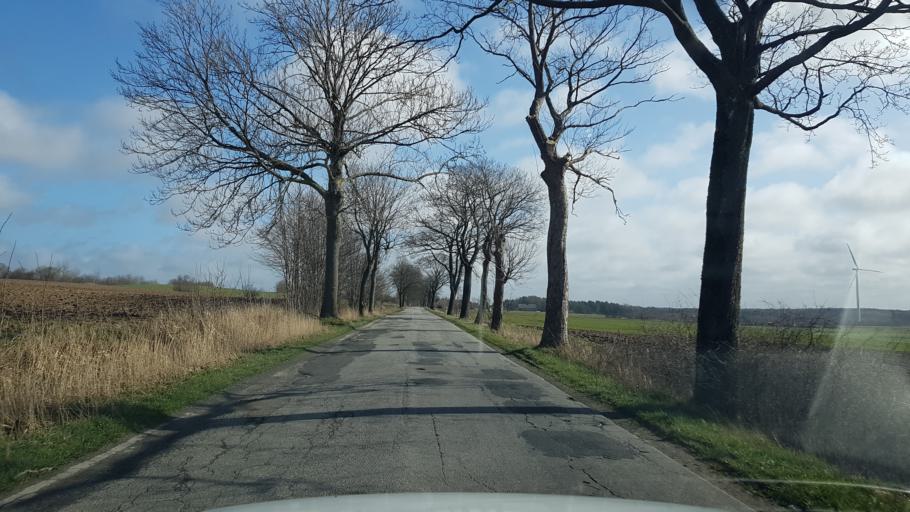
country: PL
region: West Pomeranian Voivodeship
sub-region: Powiat slawienski
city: Slawno
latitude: 54.4725
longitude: 16.6003
